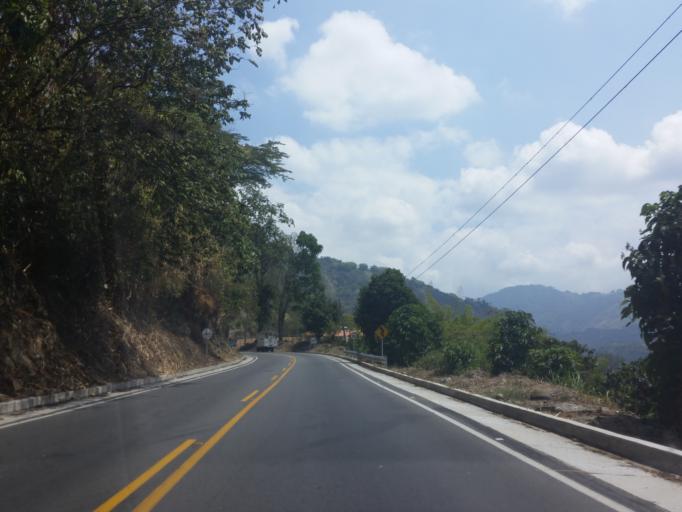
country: CO
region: Caldas
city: Chinchina
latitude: 4.9908
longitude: -75.5796
